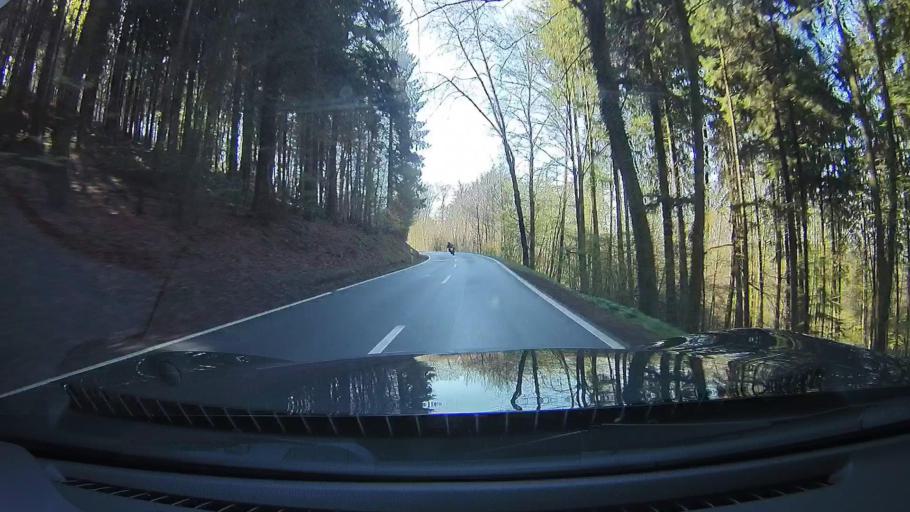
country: DE
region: Baden-Wuerttemberg
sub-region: Karlsruhe Region
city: Eberbach
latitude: 49.4379
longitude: 8.9689
